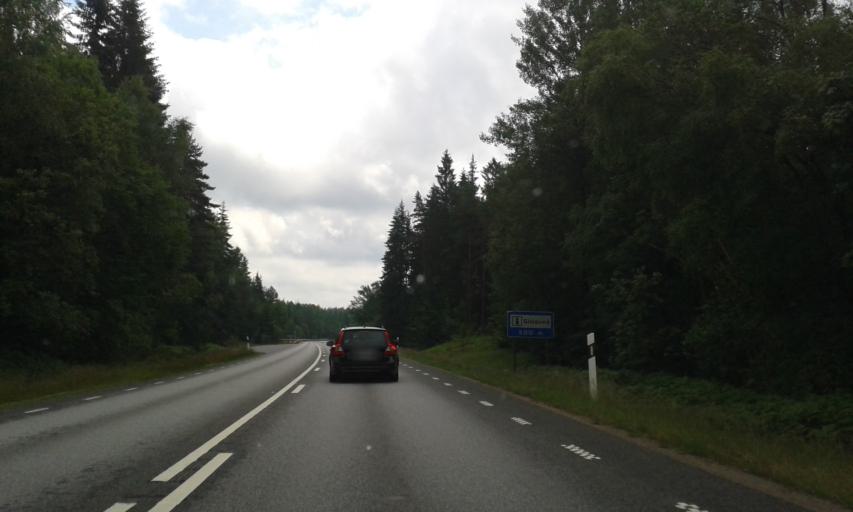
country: SE
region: Joenkoeping
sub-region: Gislaveds Kommun
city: Gislaved
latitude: 57.3390
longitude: 13.5047
